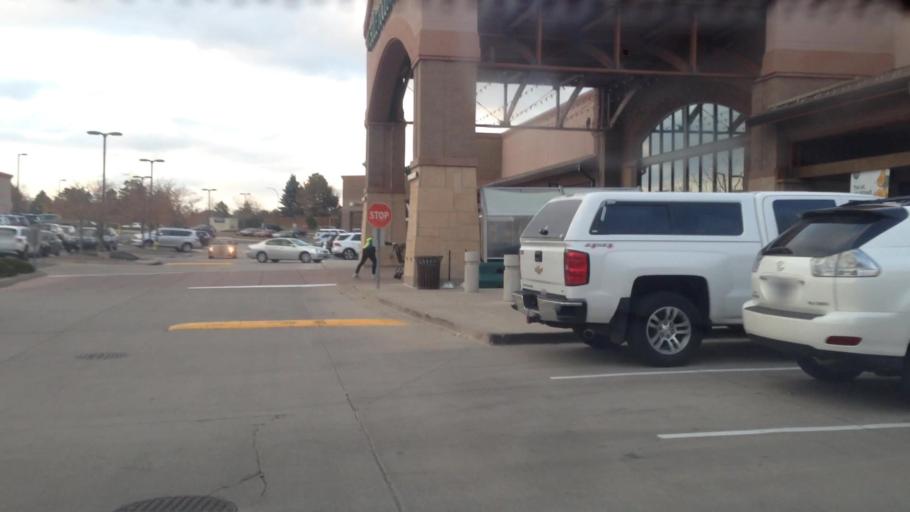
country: US
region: Colorado
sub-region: Douglas County
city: Highlands Ranch
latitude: 39.5447
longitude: -104.9426
